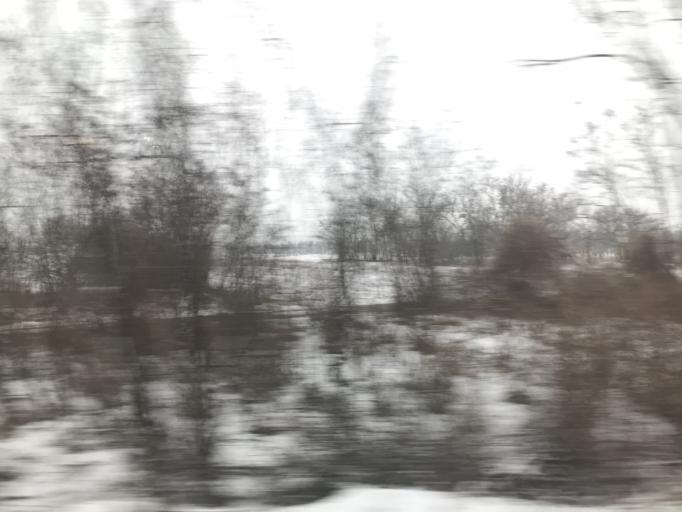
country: HU
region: Gyor-Moson-Sopron
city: Toltestava
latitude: 47.6935
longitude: 17.7802
